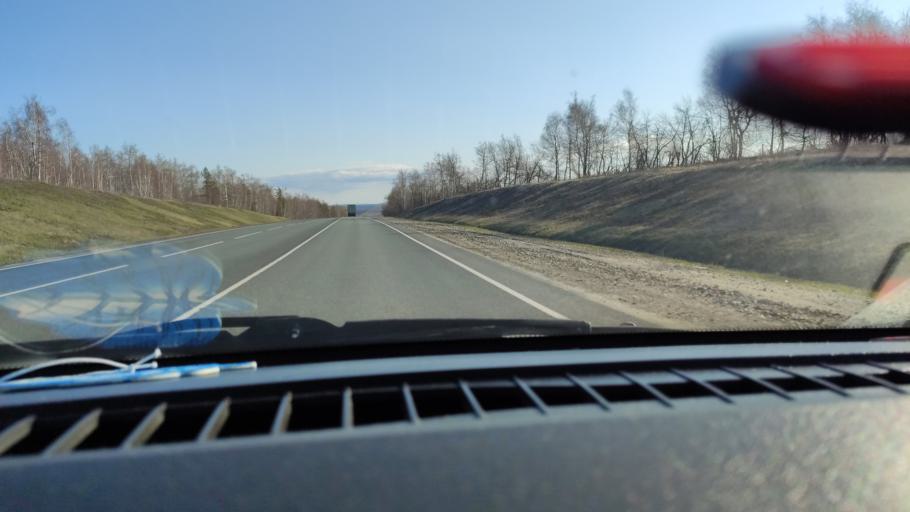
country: RU
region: Saratov
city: Khvalynsk
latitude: 52.5597
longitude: 48.0872
